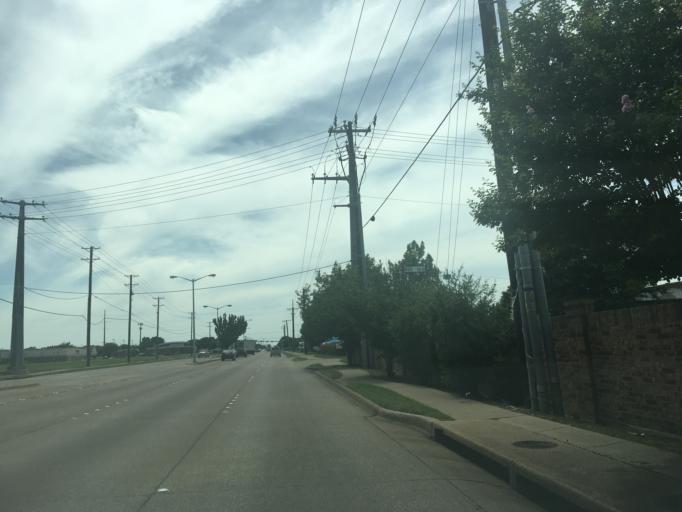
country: US
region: Texas
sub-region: Dallas County
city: Garland
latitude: 32.9313
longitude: -96.6787
